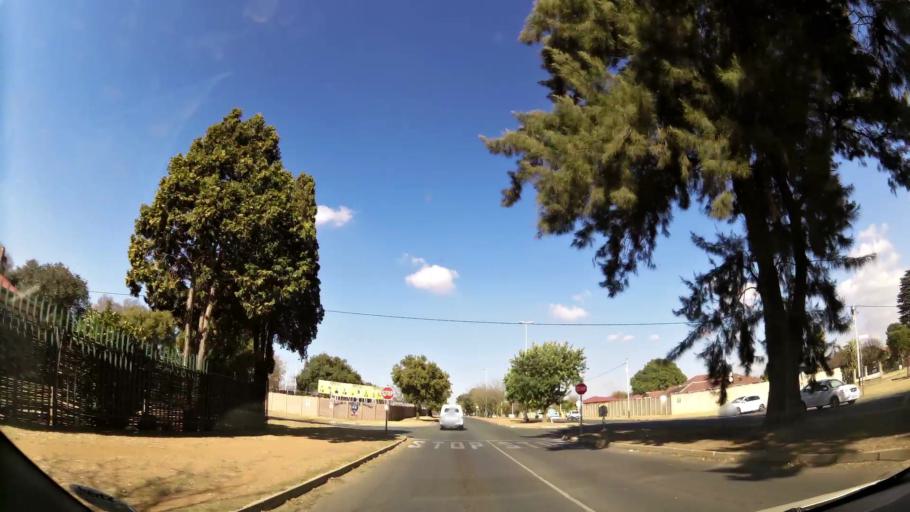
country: ZA
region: Gauteng
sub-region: City of Johannesburg Metropolitan Municipality
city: Roodepoort
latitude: -26.1367
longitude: 27.8337
